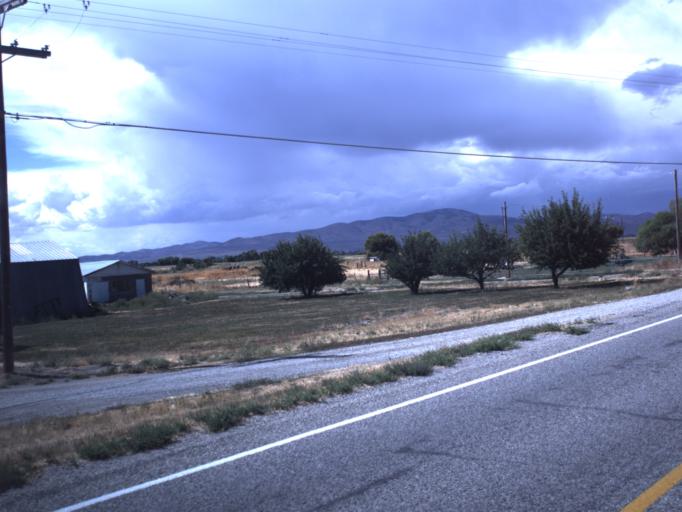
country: US
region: Utah
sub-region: Box Elder County
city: Honeyville
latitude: 41.6700
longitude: -112.0896
